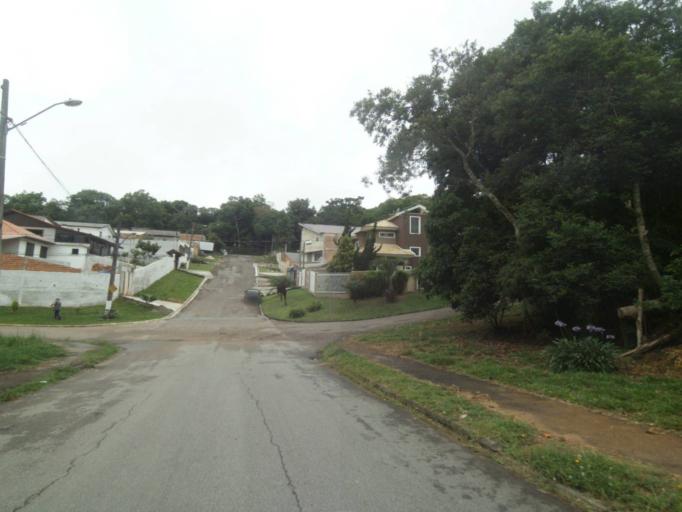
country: BR
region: Parana
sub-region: Curitiba
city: Curitiba
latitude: -25.4252
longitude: -49.3373
